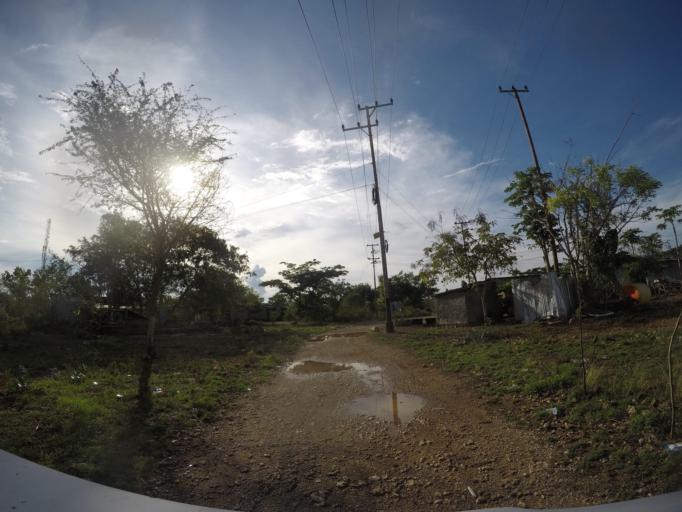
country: TL
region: Baucau
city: Baucau
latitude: -8.4865
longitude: 126.4549
